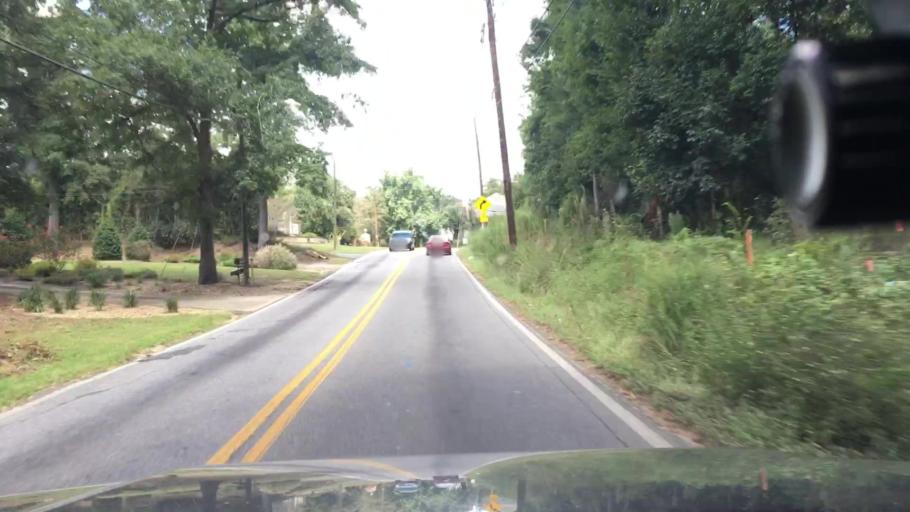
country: US
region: Georgia
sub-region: Bibb County
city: Macon
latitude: 32.8672
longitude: -83.6899
